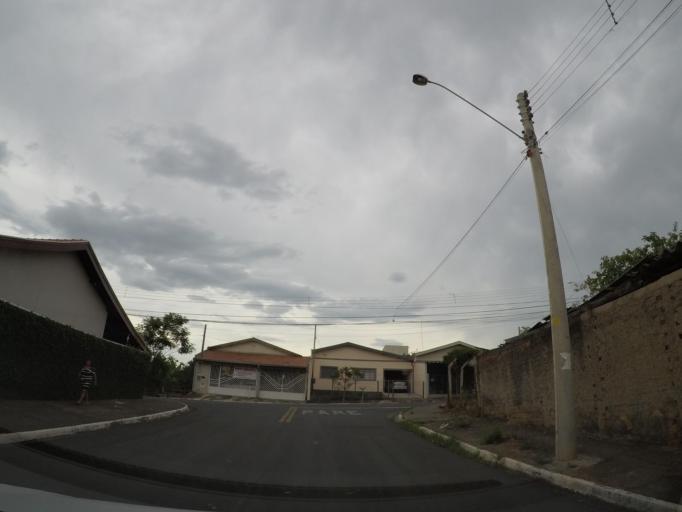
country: BR
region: Sao Paulo
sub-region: Sumare
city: Sumare
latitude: -22.8146
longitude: -47.2529
